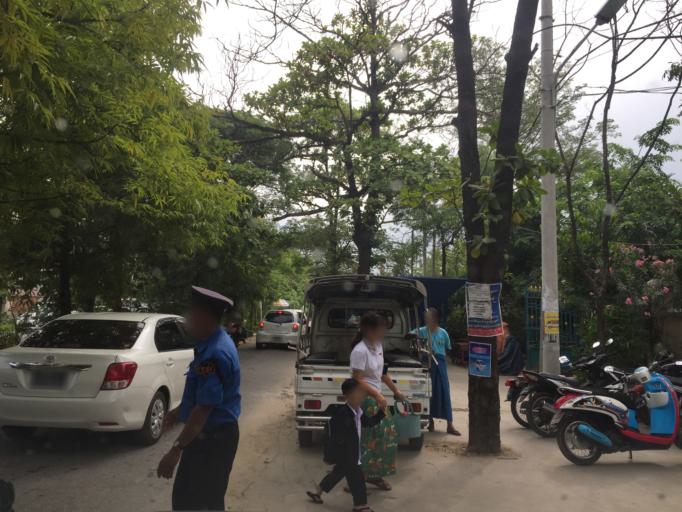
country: MM
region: Mandalay
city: Mandalay
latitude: 21.9712
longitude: 96.1082
